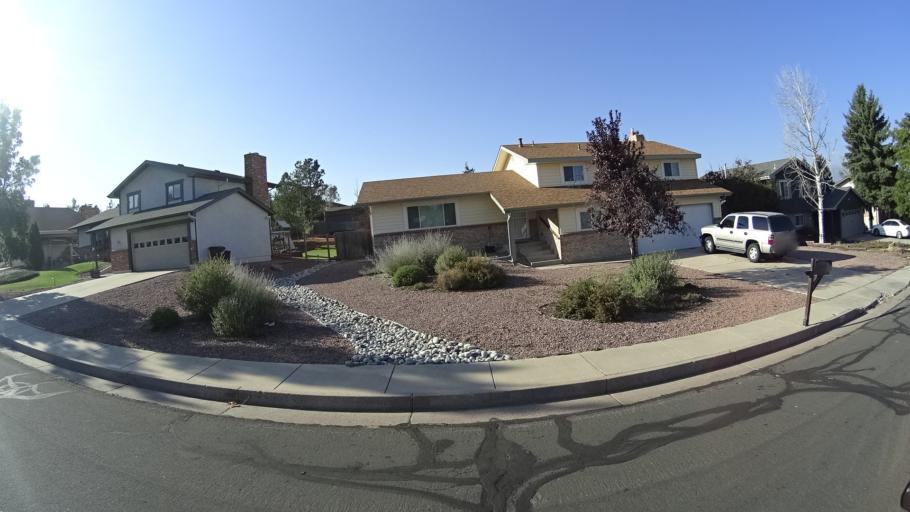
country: US
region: Colorado
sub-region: El Paso County
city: Cimarron Hills
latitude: 38.8887
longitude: -104.7325
